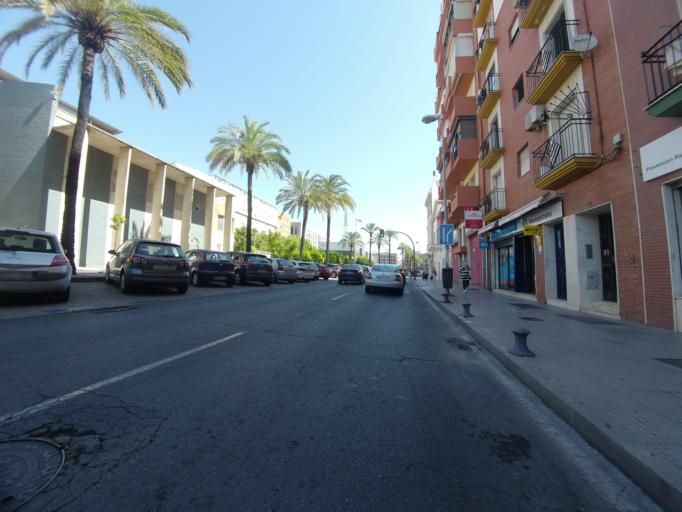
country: ES
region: Andalusia
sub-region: Provincia de Huelva
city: Huelva
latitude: 37.2583
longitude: -6.9560
